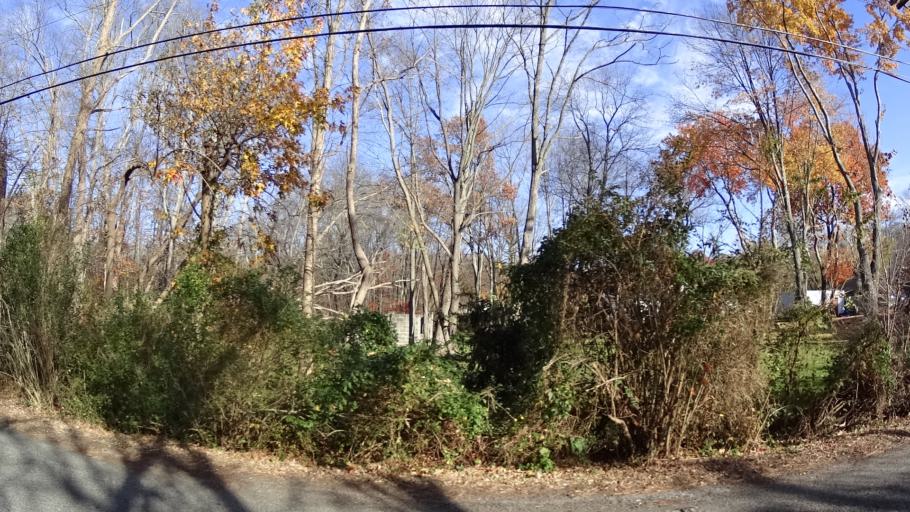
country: US
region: New Jersey
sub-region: Union County
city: Berkeley Heights
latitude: 40.6909
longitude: -74.4712
